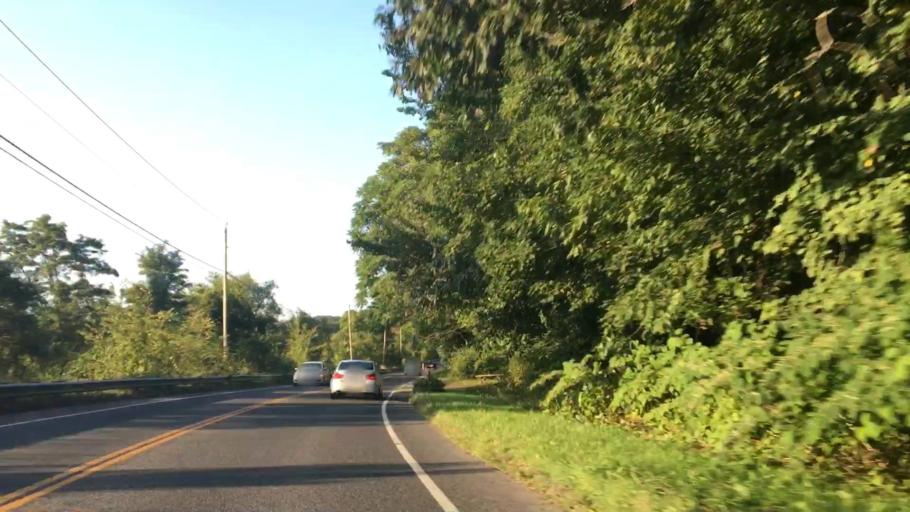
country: US
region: Connecticut
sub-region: Litchfield County
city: New Milford
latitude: 41.5575
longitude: -73.4056
